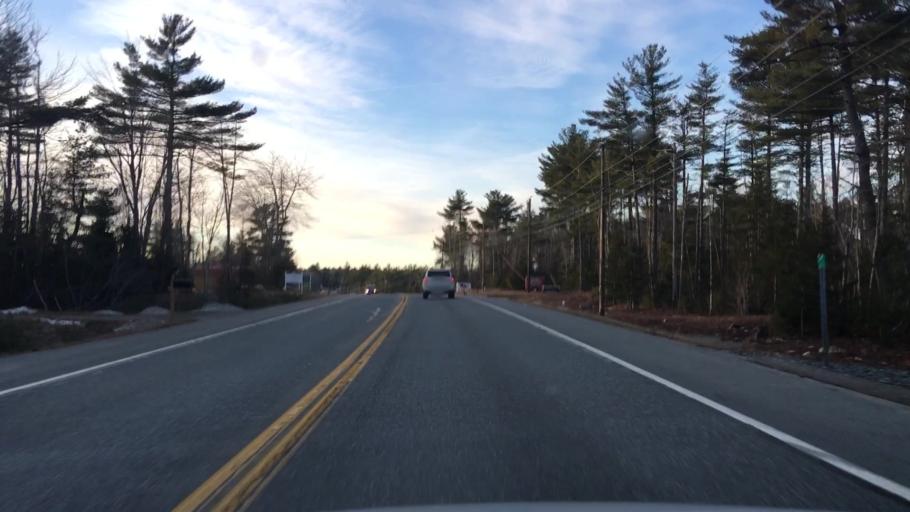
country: US
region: Maine
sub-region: Hancock County
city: Ellsworth
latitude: 44.5815
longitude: -68.4813
